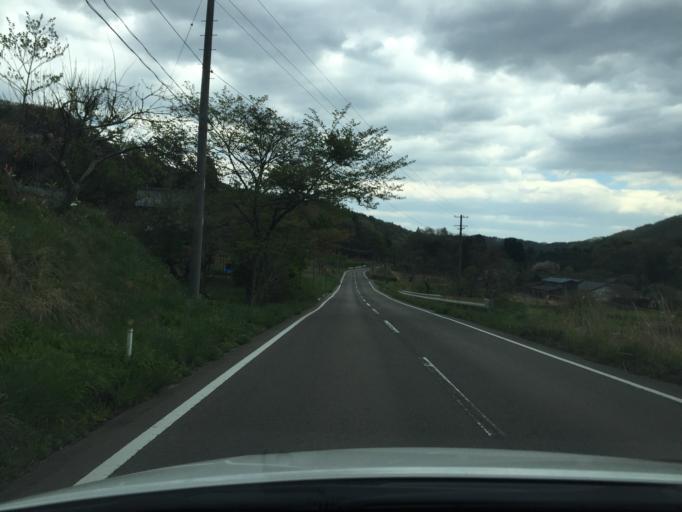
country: JP
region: Fukushima
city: Yanagawamachi-saiwaicho
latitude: 37.7481
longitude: 140.7085
